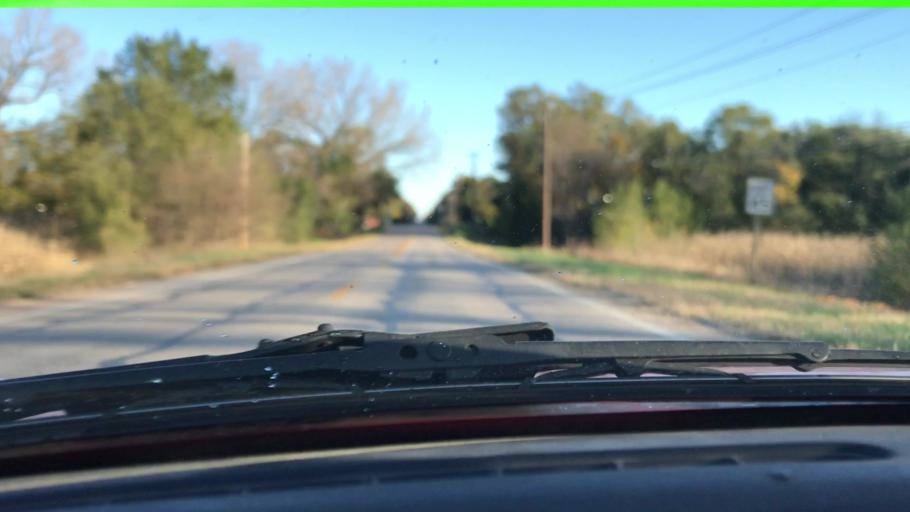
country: US
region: Nebraska
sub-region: Lancaster County
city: Lincoln
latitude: 40.7752
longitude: -96.7495
